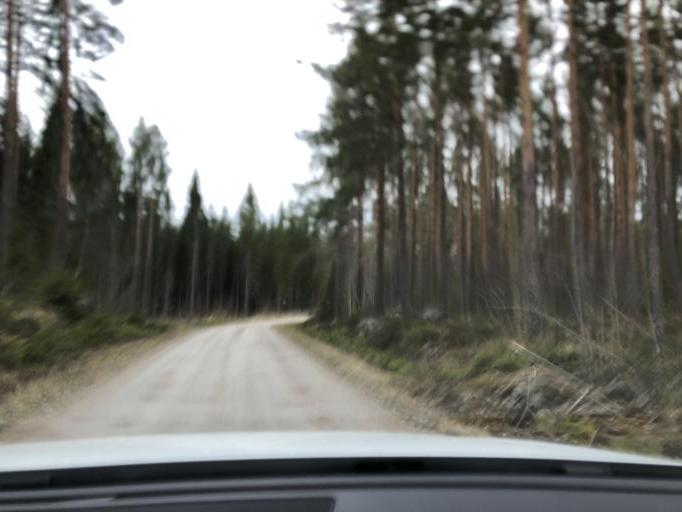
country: SE
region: Gaevleborg
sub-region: Gavle Kommun
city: Hedesunda
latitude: 60.3195
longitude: 17.1022
